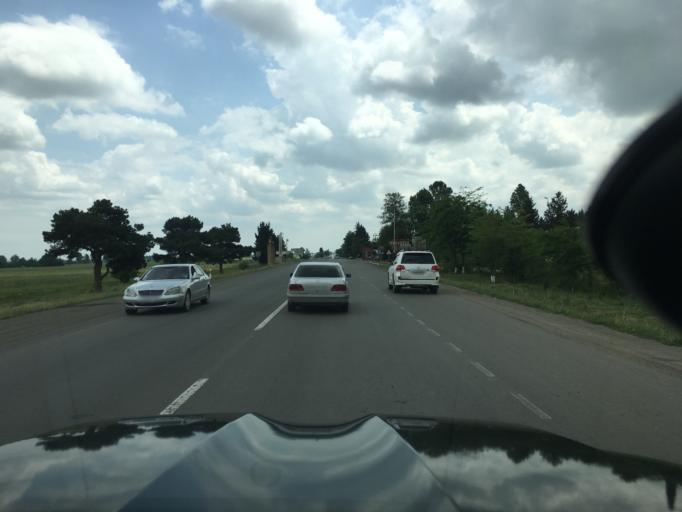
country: AZ
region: Tovuz
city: Tovuz
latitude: 40.9600
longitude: 45.7227
